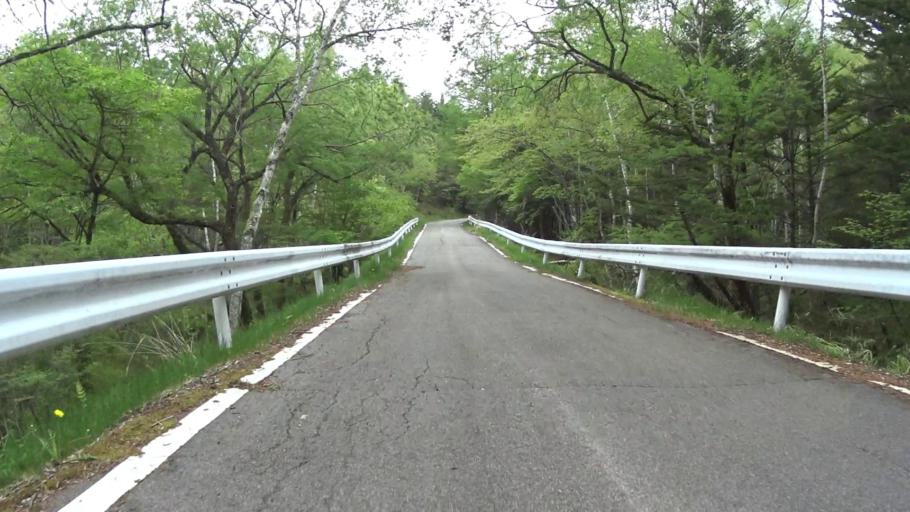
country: JP
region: Yamanashi
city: Kofu-shi
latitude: 35.8420
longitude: 138.5786
